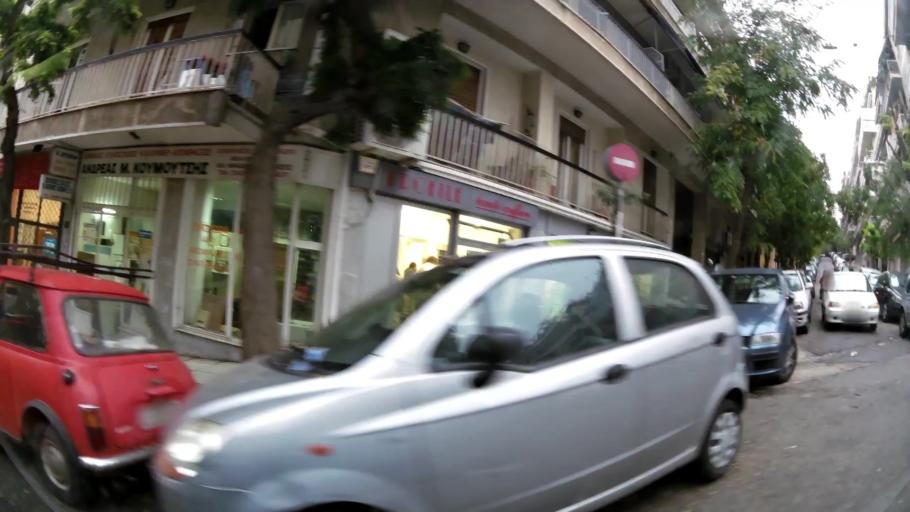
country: GR
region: Attica
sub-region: Nomarchia Athinas
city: Vyronas
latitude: 37.9702
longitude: 23.7447
